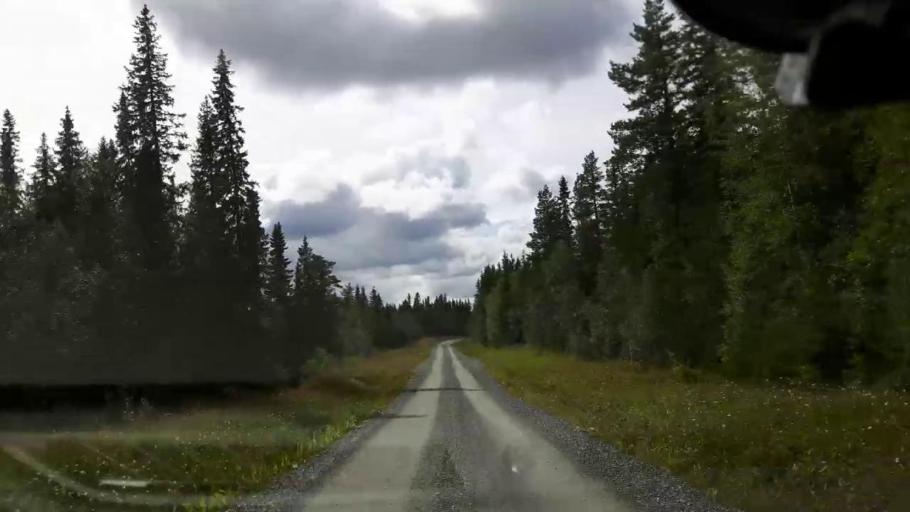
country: SE
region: Jaemtland
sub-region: Krokoms Kommun
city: Valla
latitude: 63.5717
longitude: 13.8781
